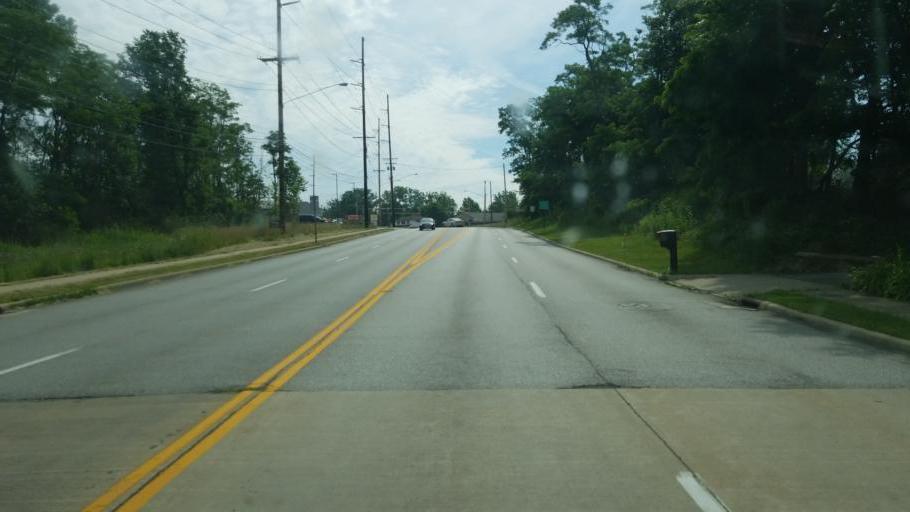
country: US
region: Ohio
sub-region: Cuyahoga County
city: Strongsville
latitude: 41.3134
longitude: -81.7880
